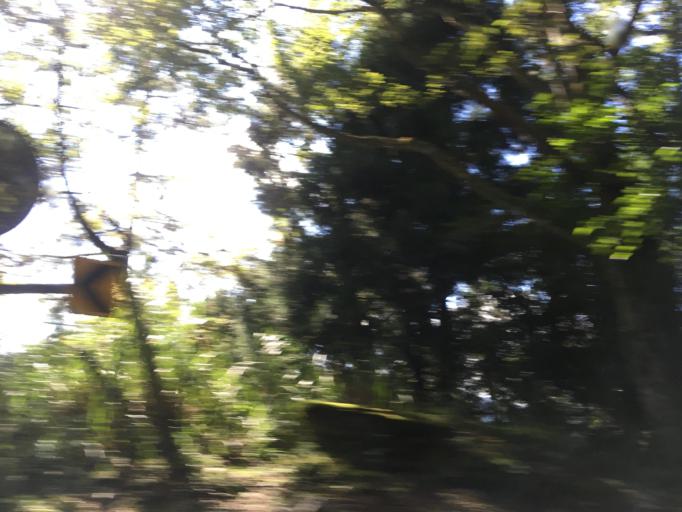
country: TW
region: Taiwan
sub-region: Yilan
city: Yilan
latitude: 24.5071
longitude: 121.5698
